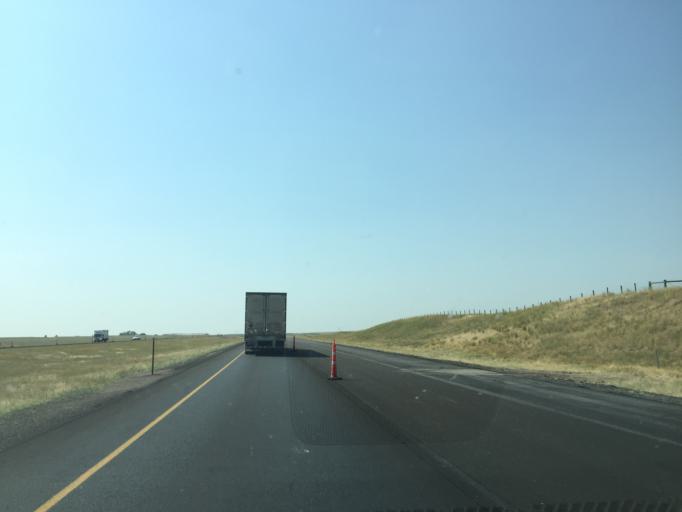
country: US
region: Wyoming
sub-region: Laramie County
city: Ranchettes
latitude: 41.3063
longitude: -104.8562
